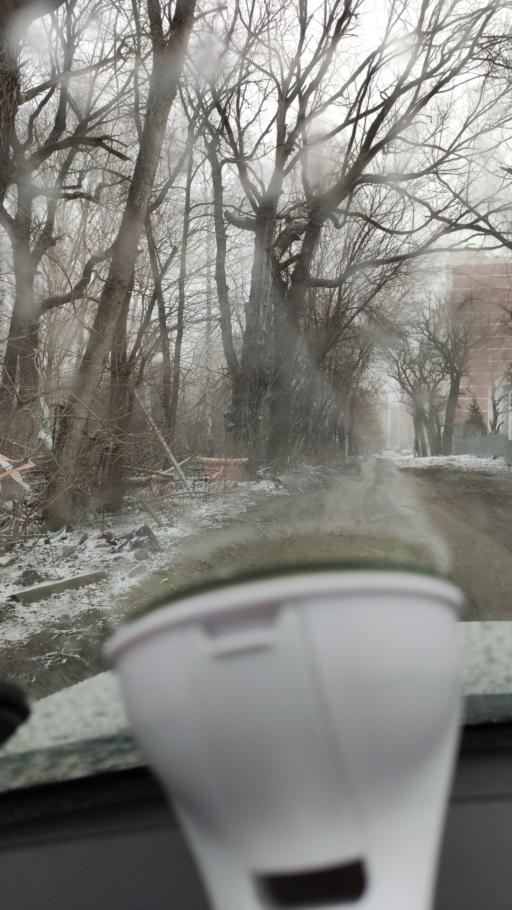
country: RU
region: Samara
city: Samara
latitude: 53.2448
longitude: 50.1779
